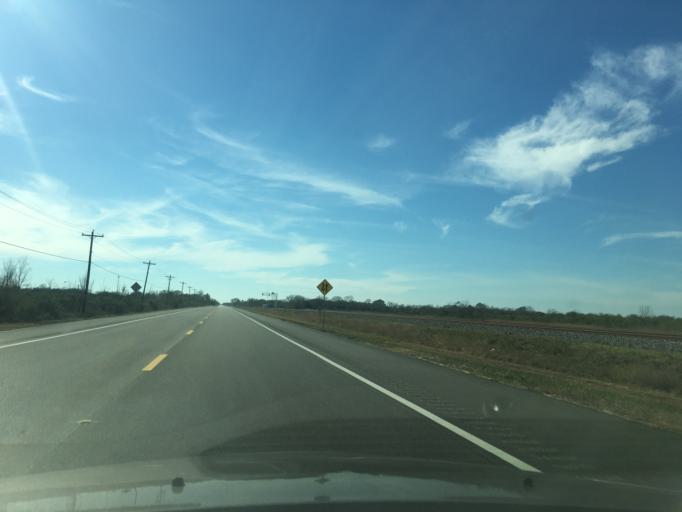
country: US
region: Texas
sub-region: Wharton County
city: East Bernard
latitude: 29.4558
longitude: -95.9864
